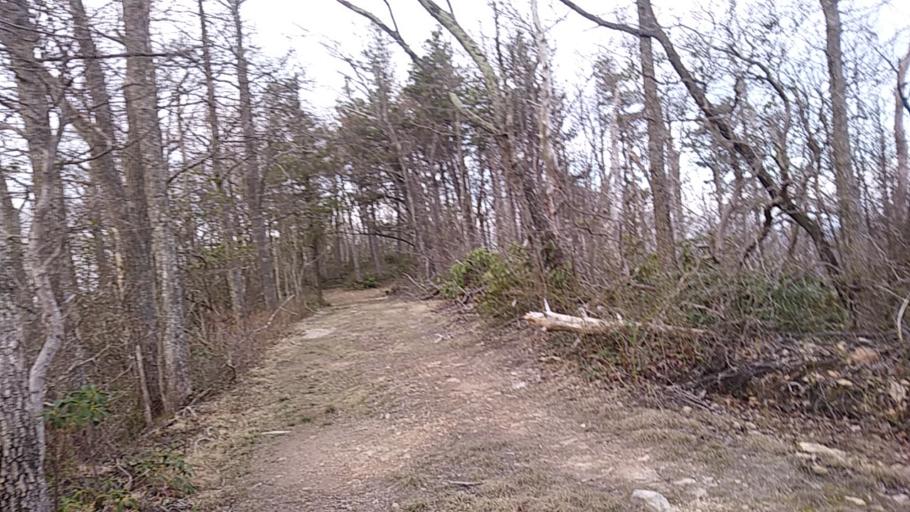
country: US
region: Tennessee
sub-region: Greene County
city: Tusculum
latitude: 36.0640
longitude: -82.6749
